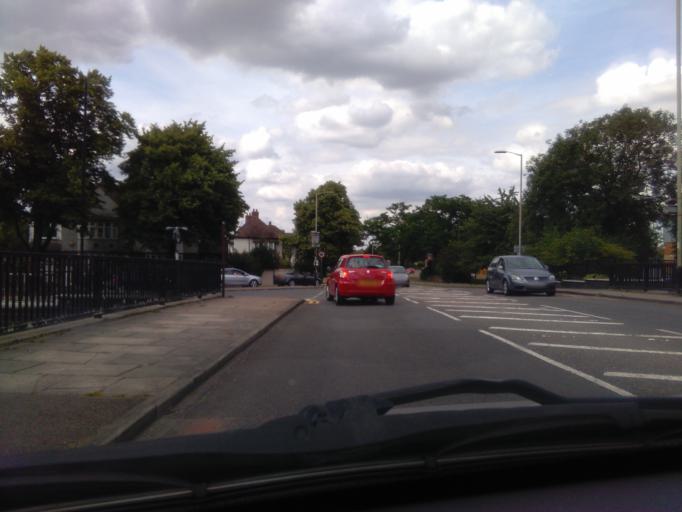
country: GB
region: England
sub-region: Bedford
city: Bedford
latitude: 52.1327
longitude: -0.4470
